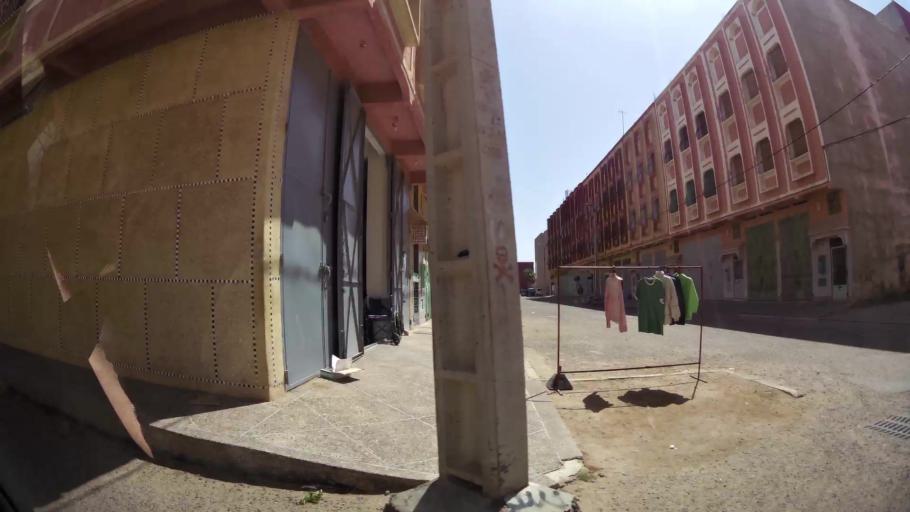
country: MA
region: Souss-Massa-Draa
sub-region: Inezgane-Ait Mellou
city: Inezgane
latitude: 30.3331
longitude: -9.5053
